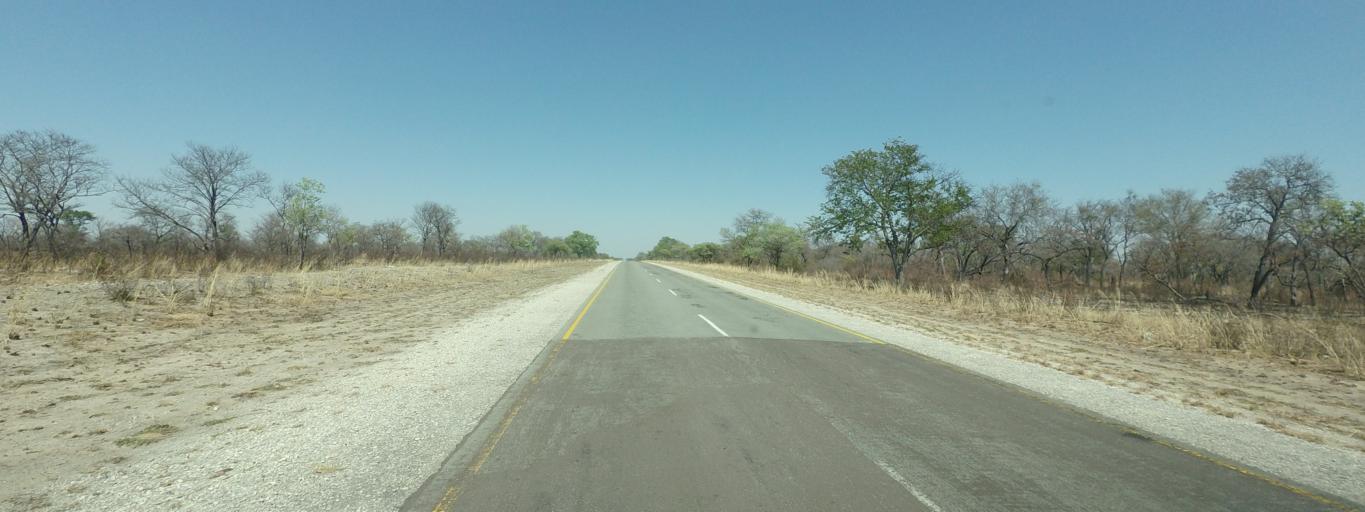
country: BW
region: North West
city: Shakawe
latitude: -17.9516
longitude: 22.5843
